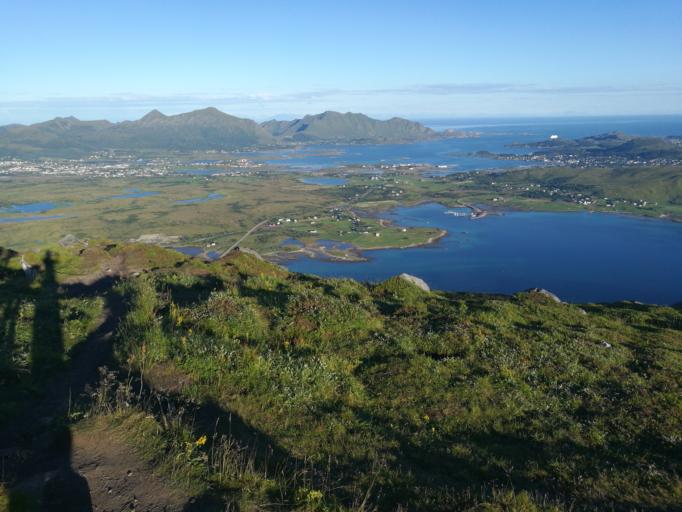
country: NO
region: Nordland
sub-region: Vestvagoy
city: Gravdal
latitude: 68.1611
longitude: 13.5018
